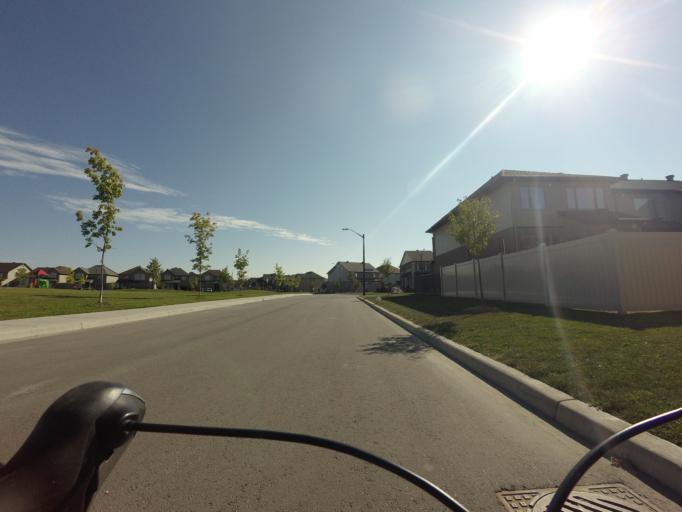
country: CA
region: Ontario
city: Bells Corners
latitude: 45.2675
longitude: -75.6964
